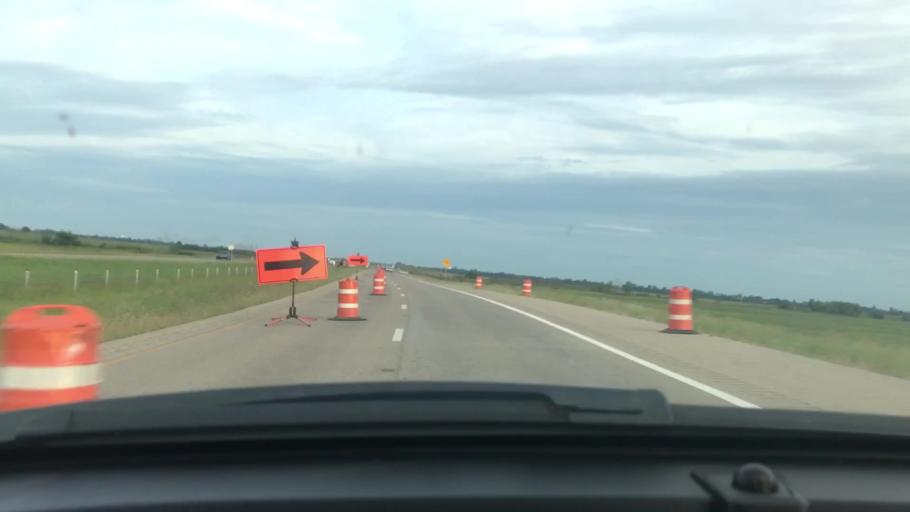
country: US
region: Arkansas
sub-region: Craighead County
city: Bay
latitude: 35.7164
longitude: -90.5795
